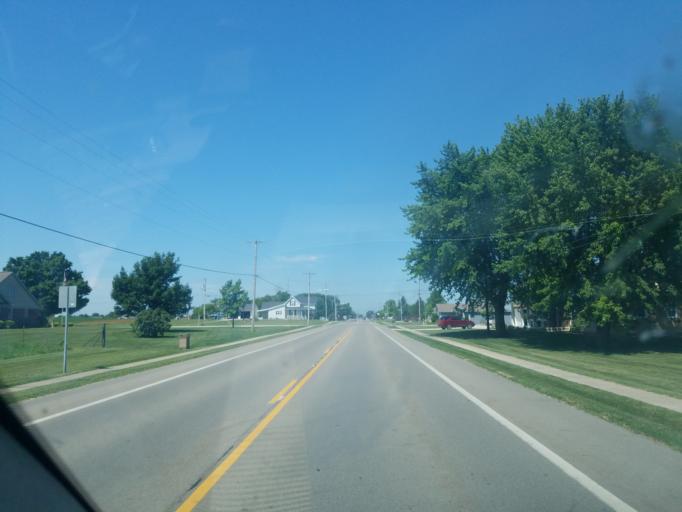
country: US
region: Ohio
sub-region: Auglaize County
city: New Bremen
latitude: 40.4077
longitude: -84.4828
